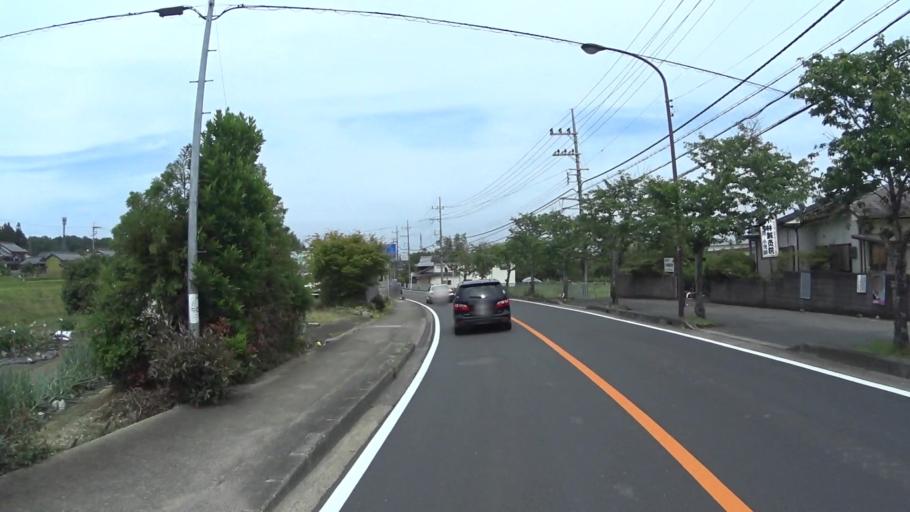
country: JP
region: Shiga Prefecture
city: Kitahama
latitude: 35.1333
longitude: 135.8998
